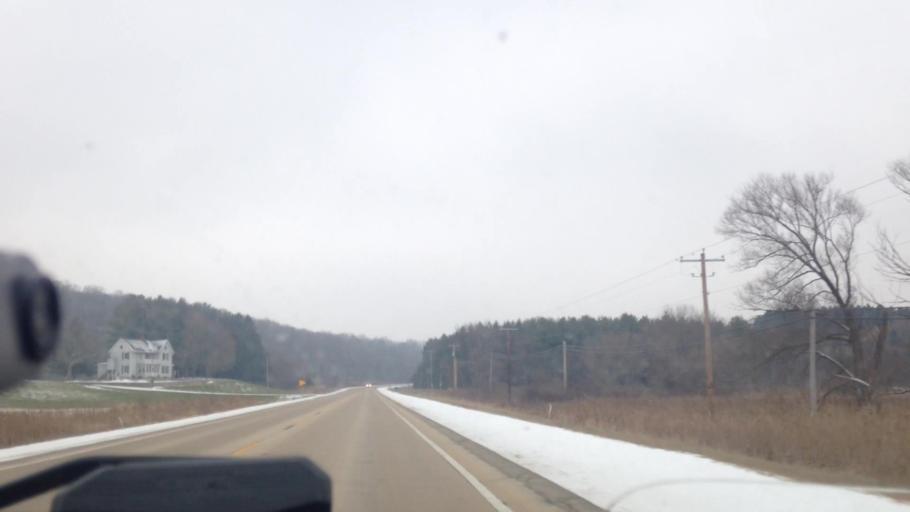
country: US
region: Wisconsin
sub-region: Dodge County
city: Mayville
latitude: 43.4592
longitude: -88.5441
